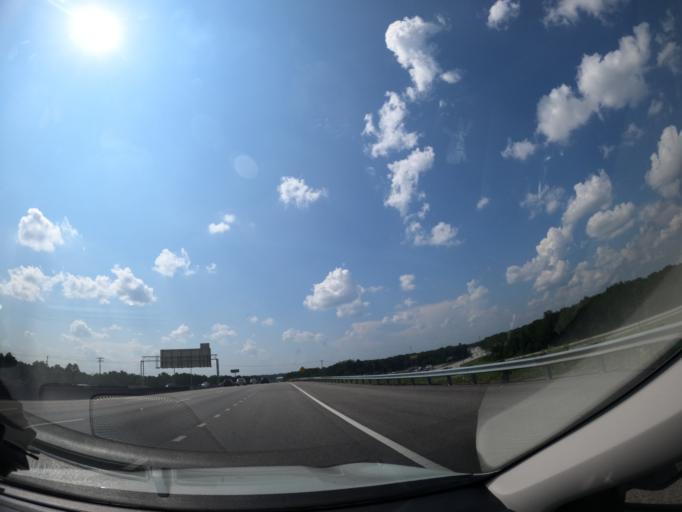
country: US
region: South Carolina
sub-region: Lexington County
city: Cayce
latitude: 33.9325
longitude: -81.0761
